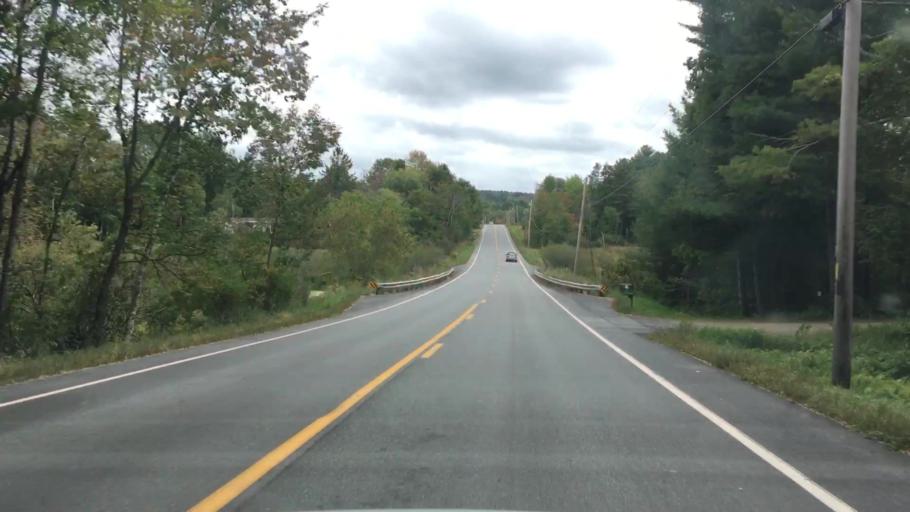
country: US
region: Maine
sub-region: Penobscot County
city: Hermon
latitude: 44.7515
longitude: -68.9706
